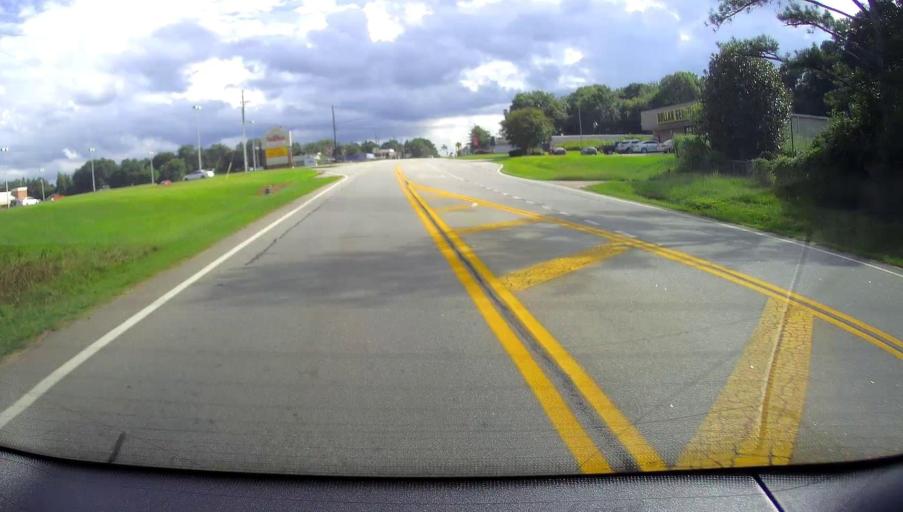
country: US
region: Georgia
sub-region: Meriwether County
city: Manchester
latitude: 32.9864
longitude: -84.5737
